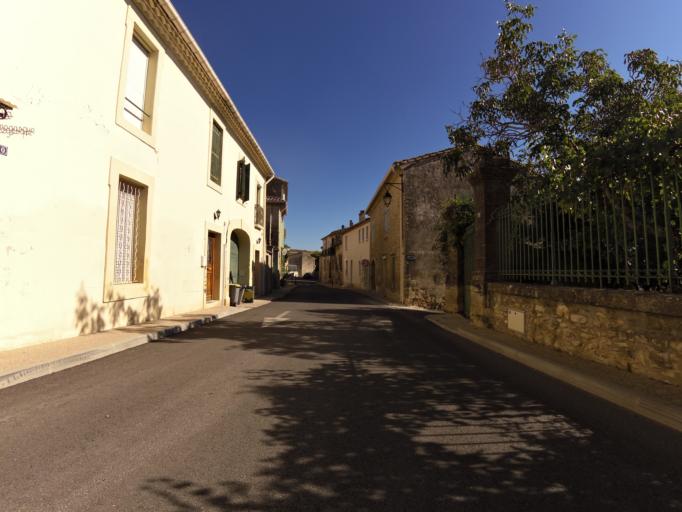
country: FR
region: Languedoc-Roussillon
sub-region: Departement du Gard
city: Aubais
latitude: 43.7562
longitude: 4.1485
